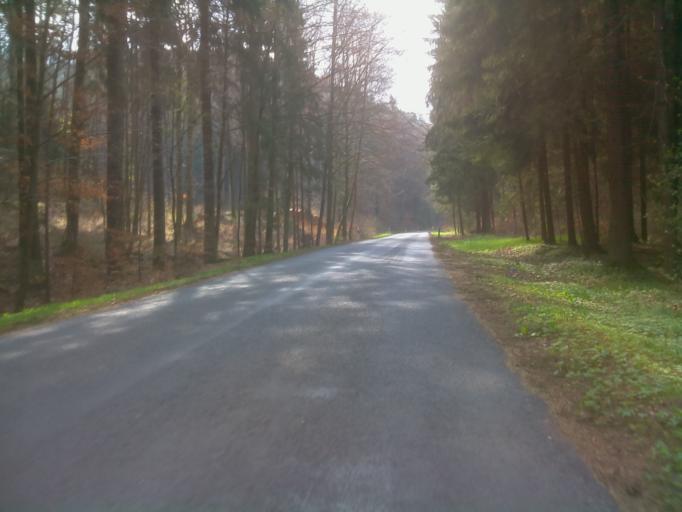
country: DE
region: Thuringia
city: Grosseutersdorf
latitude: 50.7725
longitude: 11.5637
